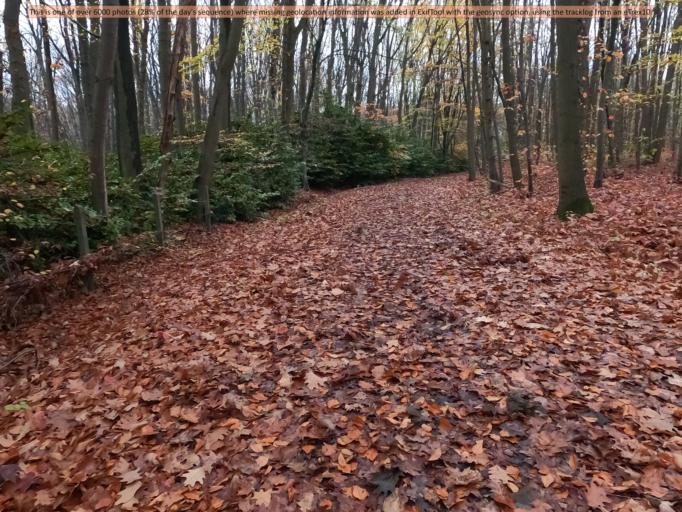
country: BE
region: Flanders
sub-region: Provincie Antwerpen
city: Nijlen
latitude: 51.1304
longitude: 4.7077
